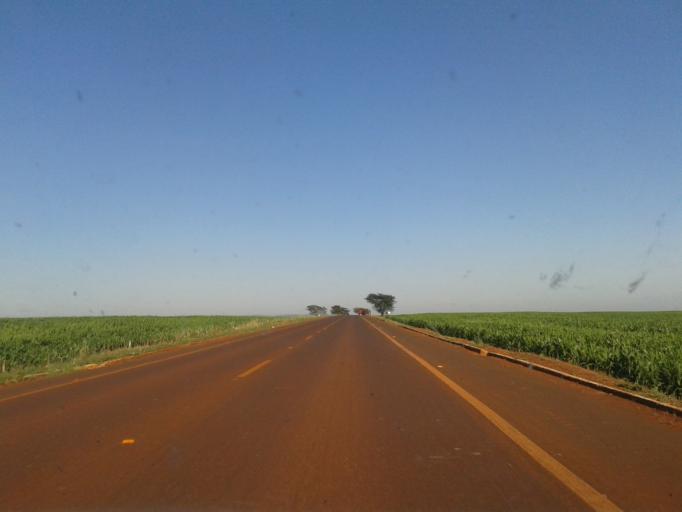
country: BR
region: Minas Gerais
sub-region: Capinopolis
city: Capinopolis
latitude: -18.6980
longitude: -49.6388
